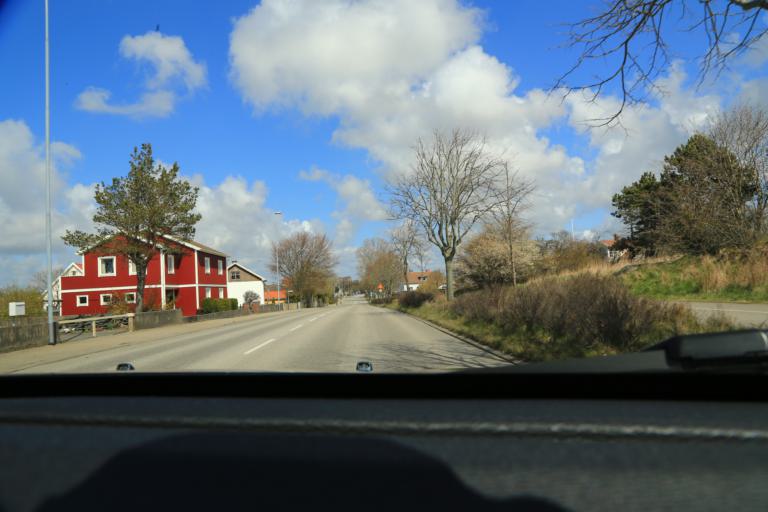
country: SE
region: Halland
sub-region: Varbergs Kommun
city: Varberg
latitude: 57.1071
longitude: 12.2734
